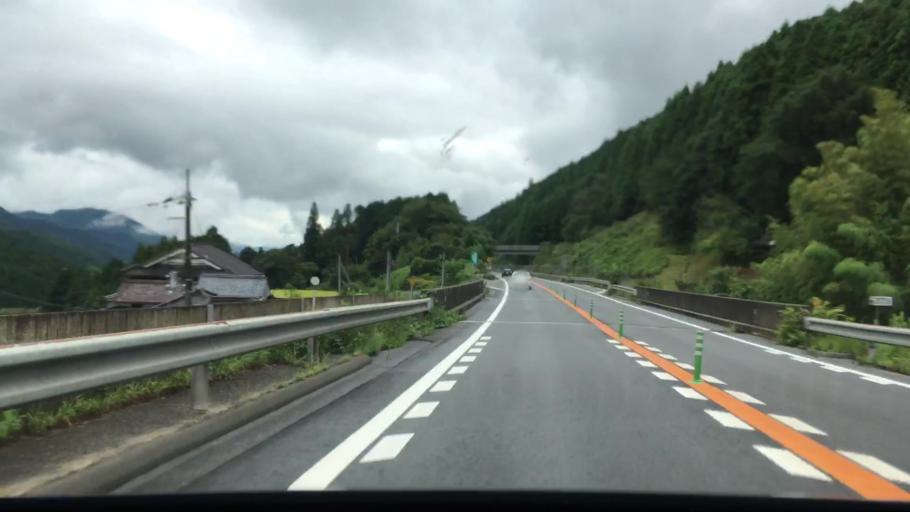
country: JP
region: Hyogo
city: Nishiwaki
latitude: 35.1090
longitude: 134.7803
